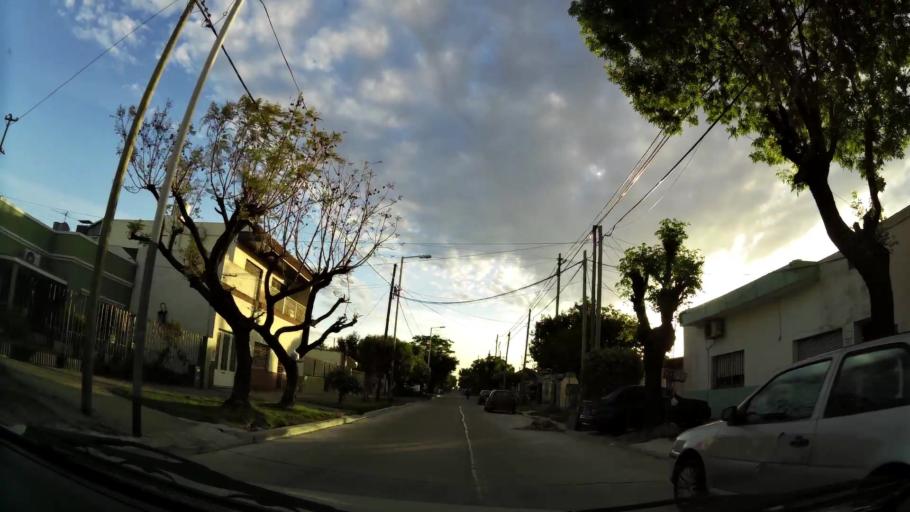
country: AR
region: Buenos Aires
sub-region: Partido de Avellaneda
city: Avellaneda
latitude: -34.7072
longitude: -58.3401
